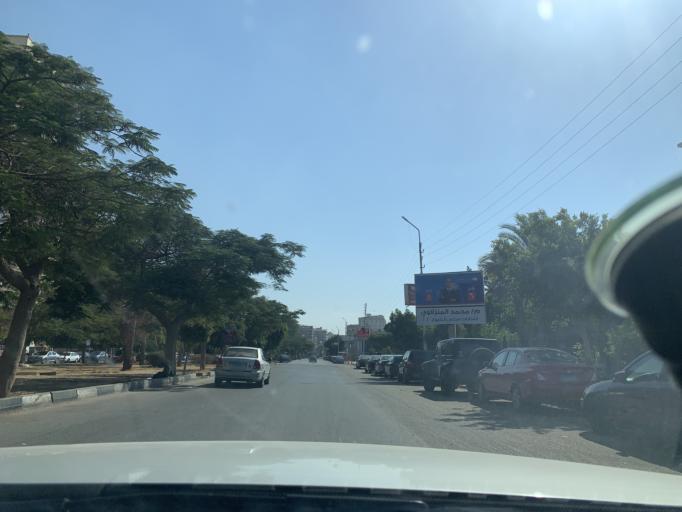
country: EG
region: Muhafazat al Qalyubiyah
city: Al Khankah
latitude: 30.1167
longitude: 31.3462
